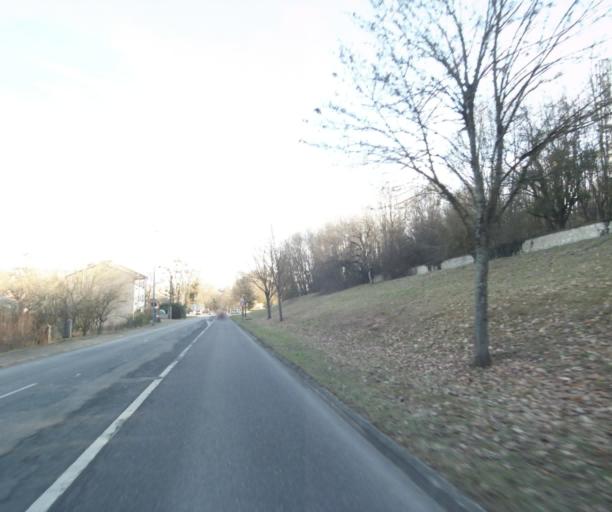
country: FR
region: Lorraine
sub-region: Departement de Meurthe-et-Moselle
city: Villers-les-Nancy
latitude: 48.6665
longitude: 6.1456
